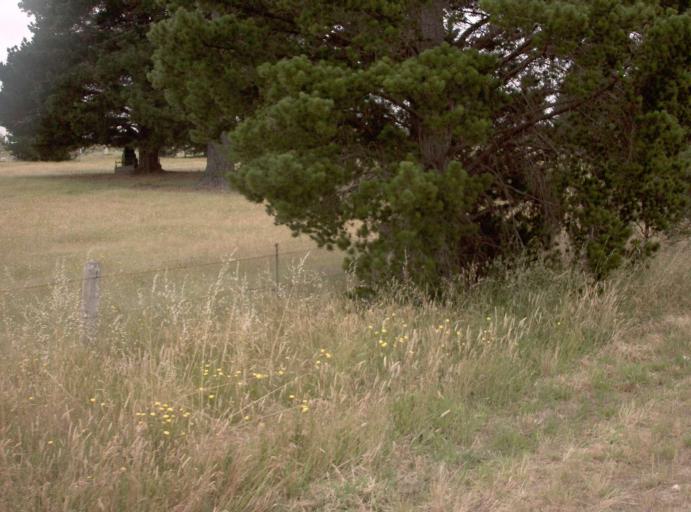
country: AU
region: Victoria
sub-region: East Gippsland
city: Bairnsdale
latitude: -37.8216
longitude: 147.4353
